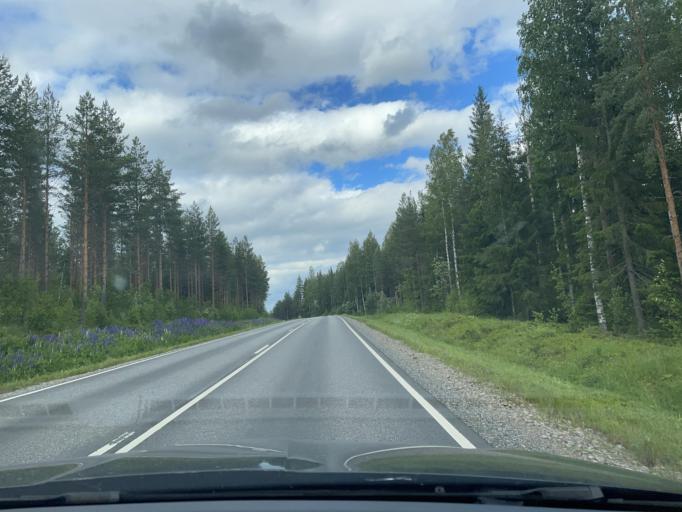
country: FI
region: Central Finland
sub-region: Jyvaeskylae
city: Petaejaevesi
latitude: 62.2187
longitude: 25.1539
